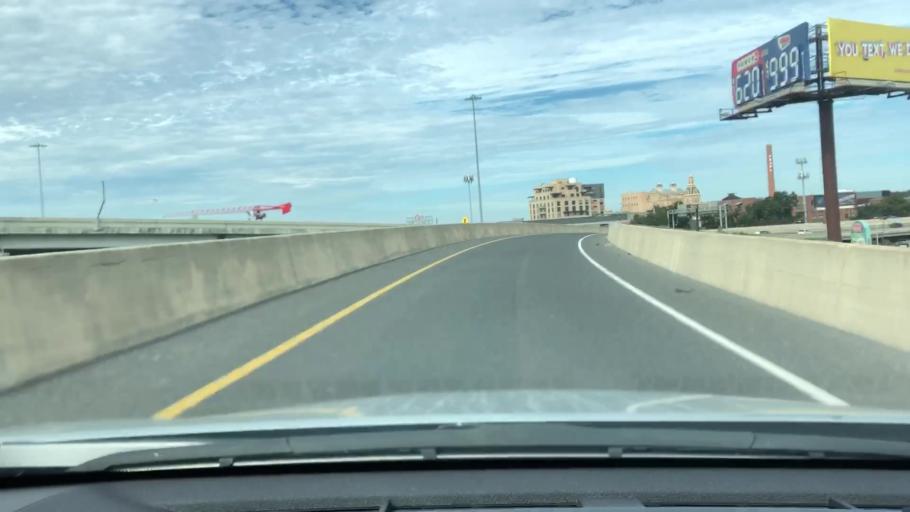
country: US
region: Texas
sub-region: Bexar County
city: San Antonio
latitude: 29.4392
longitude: -98.4771
